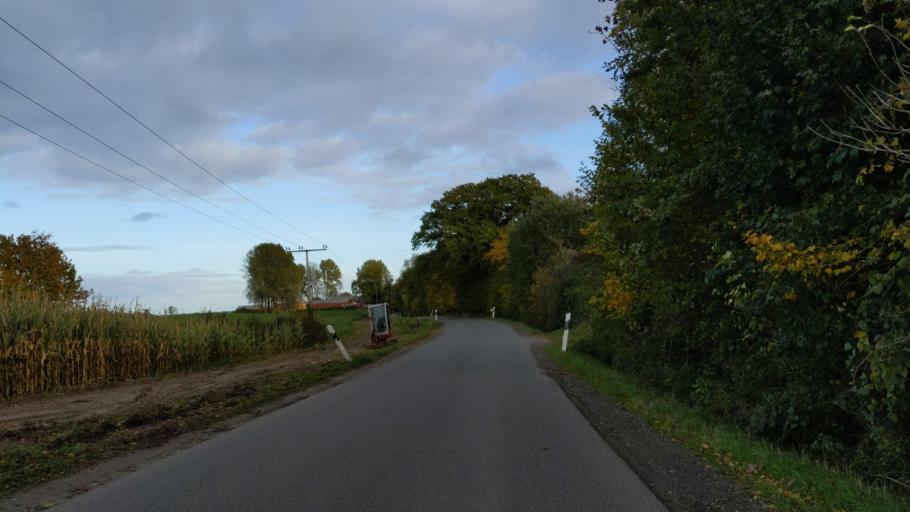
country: DE
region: Schleswig-Holstein
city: Susel
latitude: 54.1016
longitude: 10.7282
